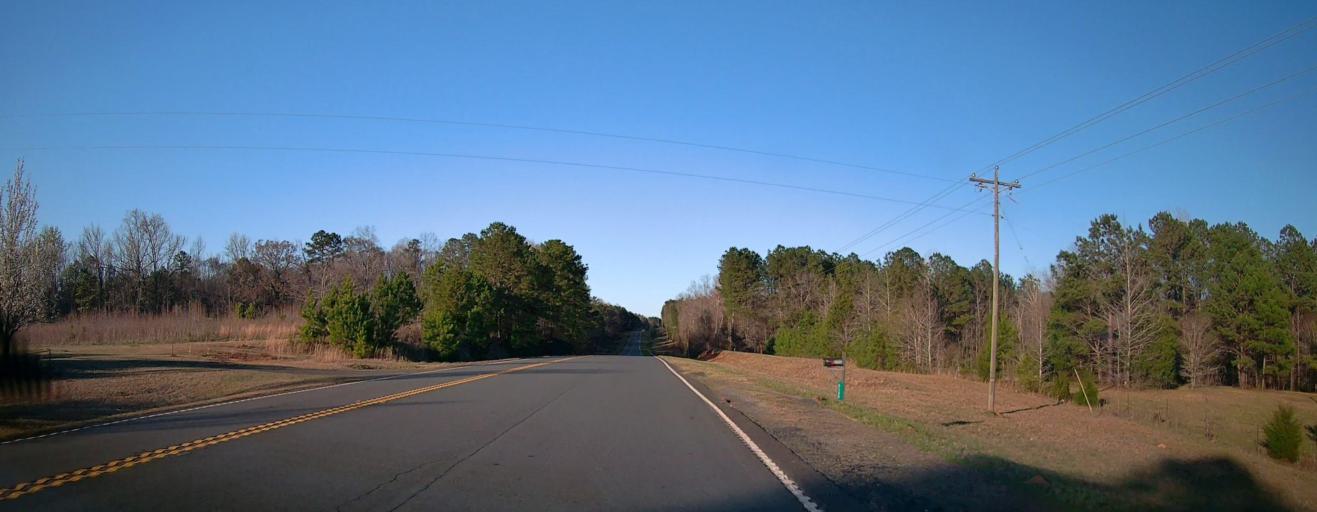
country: US
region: Georgia
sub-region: Talbot County
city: Talbotton
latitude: 32.6103
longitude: -84.5526
